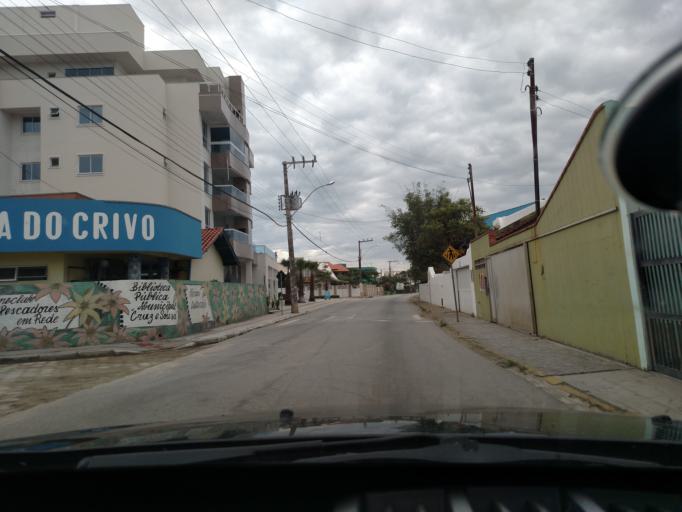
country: BR
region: Santa Catarina
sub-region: Porto Belo
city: Porto Belo
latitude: -27.1817
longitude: -48.5201
